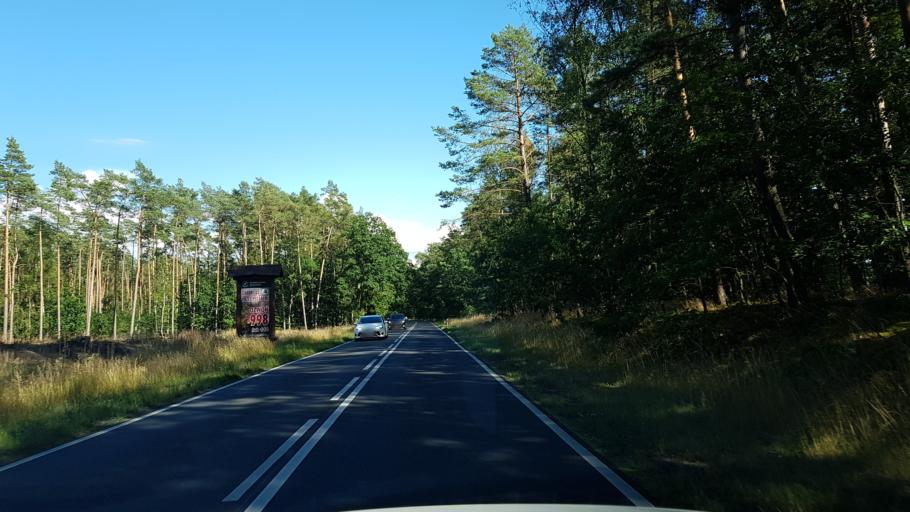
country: PL
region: West Pomeranian Voivodeship
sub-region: Powiat goleniowski
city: Stepnica
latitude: 53.6262
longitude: 14.6830
